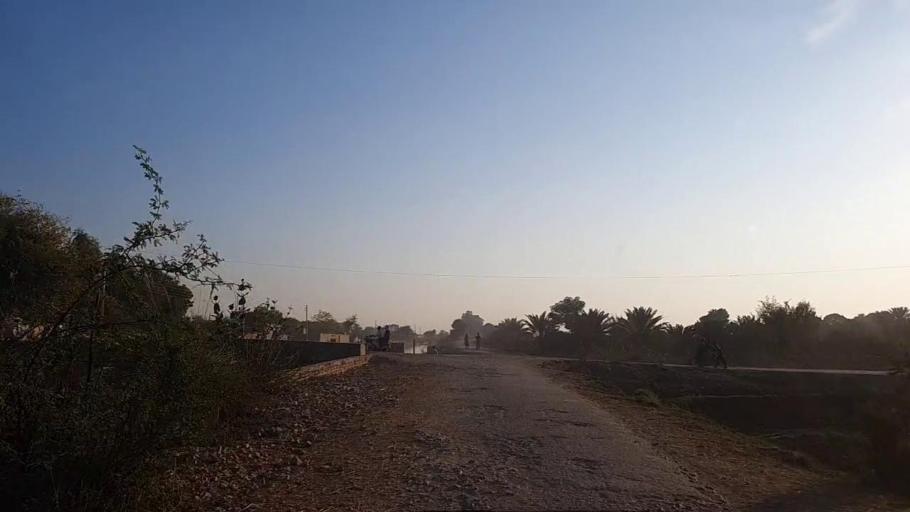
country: PK
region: Sindh
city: Sobhadero
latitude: 27.3882
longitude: 68.3830
